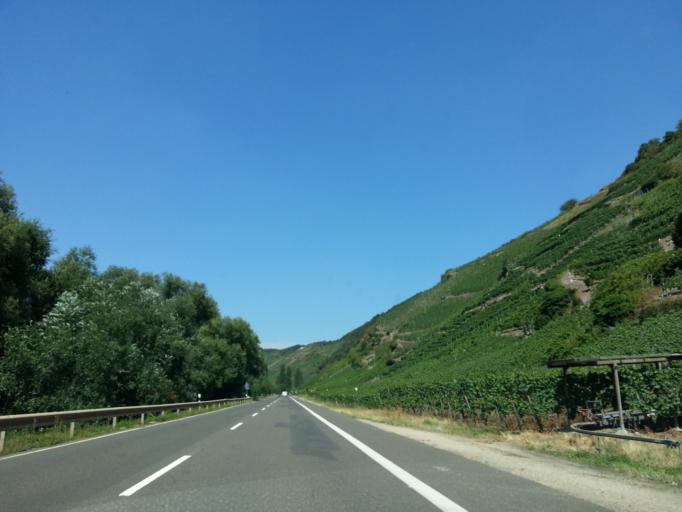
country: DE
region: Rheinland-Pfalz
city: Kowerich
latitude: 49.8276
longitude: 6.8852
